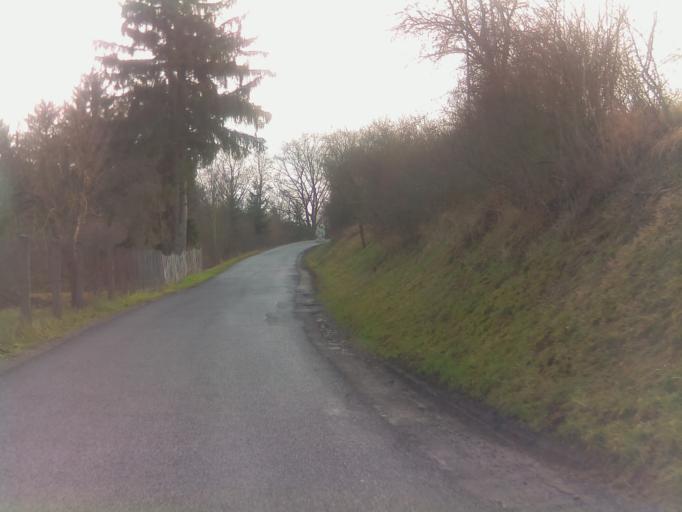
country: DE
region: Thuringia
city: Utendorf
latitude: 50.6022
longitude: 10.4388
